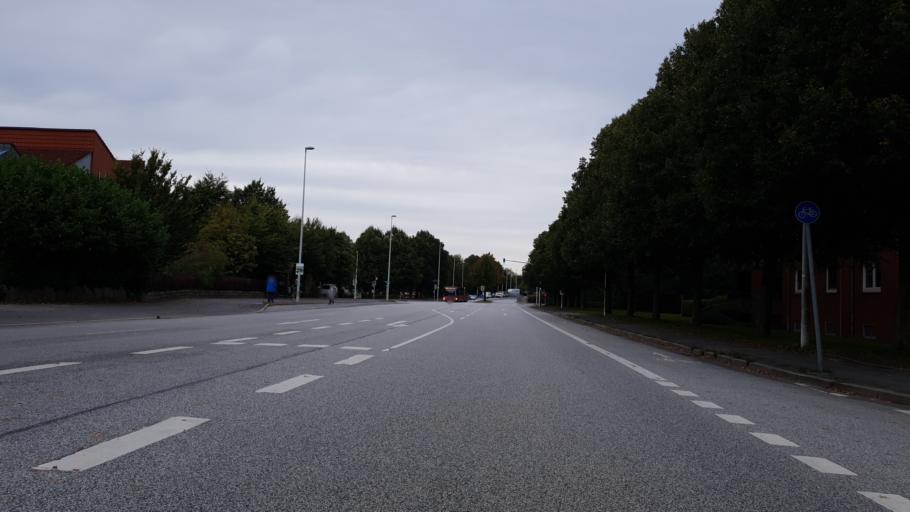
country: DE
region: Schleswig-Holstein
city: Kronshagen
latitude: 54.3585
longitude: 10.0821
